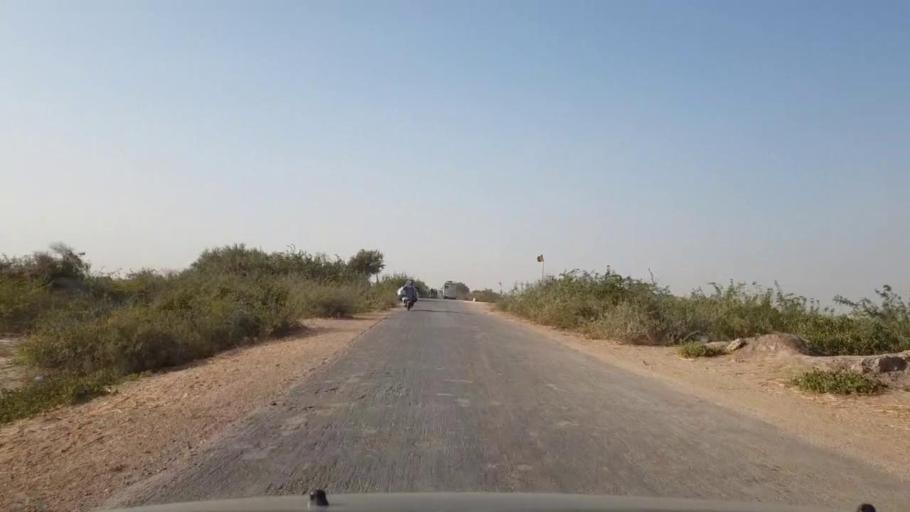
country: PK
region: Sindh
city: Tando Ghulam Ali
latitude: 25.1508
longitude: 68.8597
